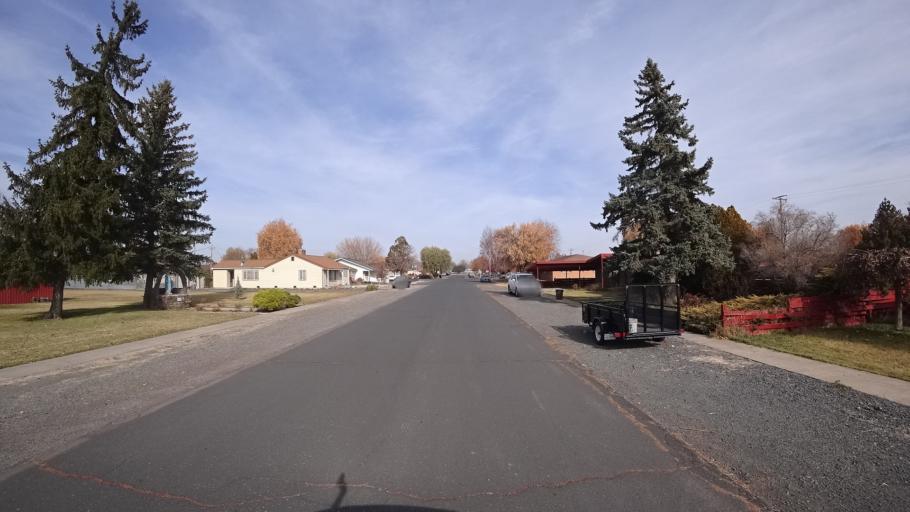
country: US
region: California
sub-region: Siskiyou County
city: Tulelake
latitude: 41.9514
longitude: -121.4792
